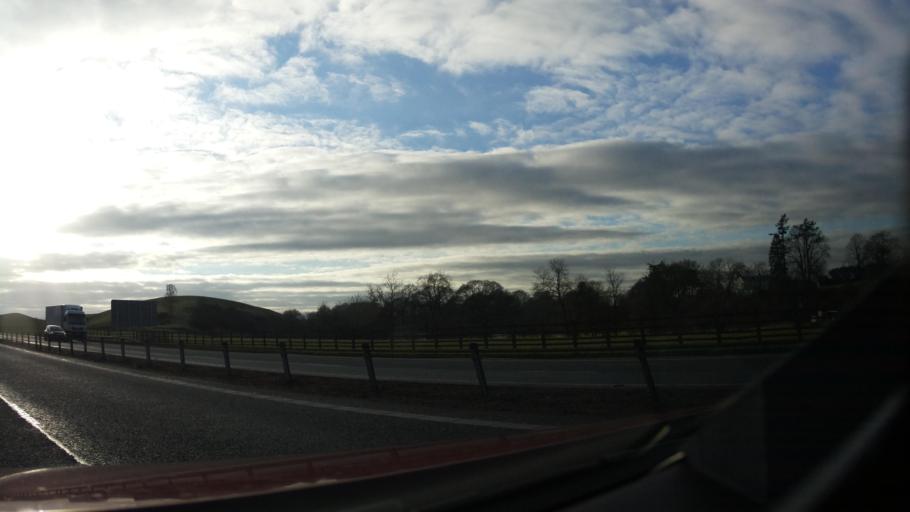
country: GB
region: Scotland
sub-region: Dumfries and Galloway
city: Lochmaben
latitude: 55.2087
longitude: -3.4125
